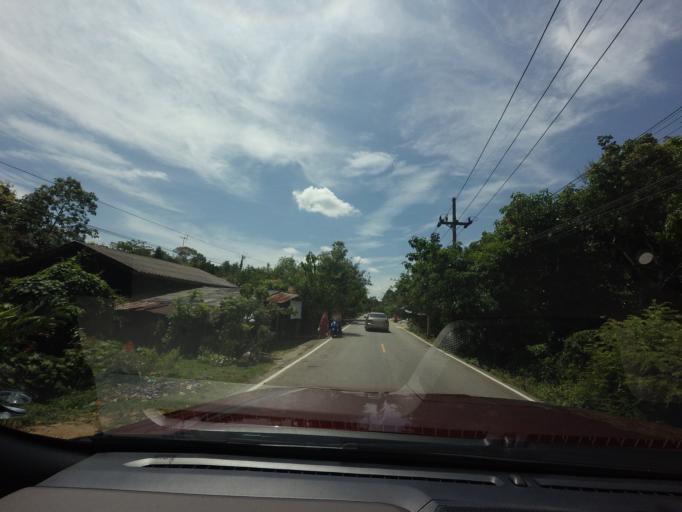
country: TH
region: Narathiwat
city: Ra-ngae
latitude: 6.2859
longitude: 101.6846
